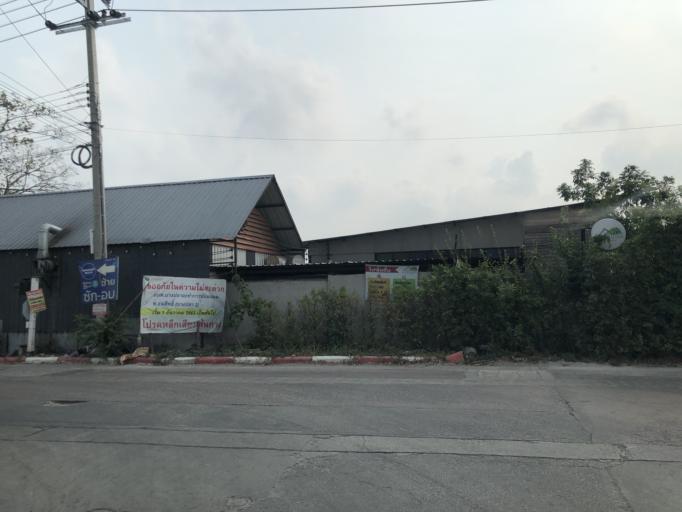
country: TH
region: Samut Prakan
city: Bang Bo District
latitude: 13.5810
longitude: 100.7217
